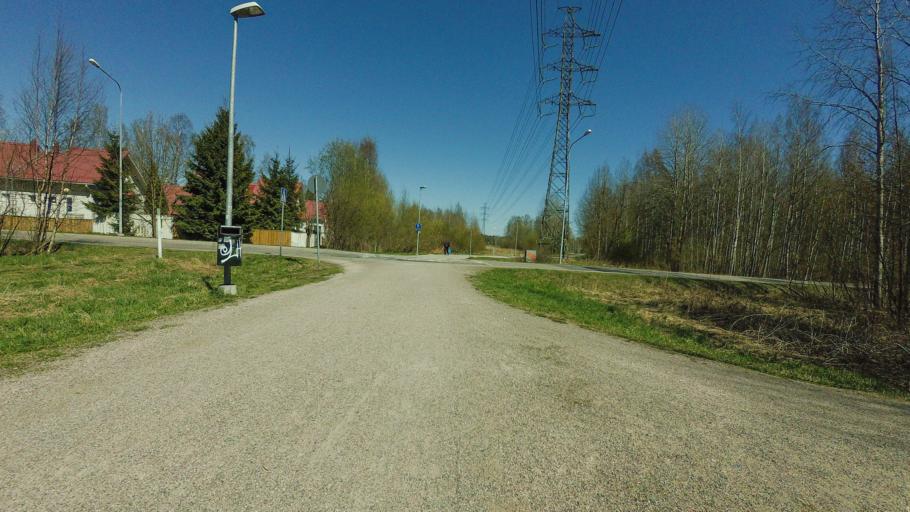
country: FI
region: Uusimaa
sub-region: Helsinki
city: Vantaa
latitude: 60.2285
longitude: 25.1008
